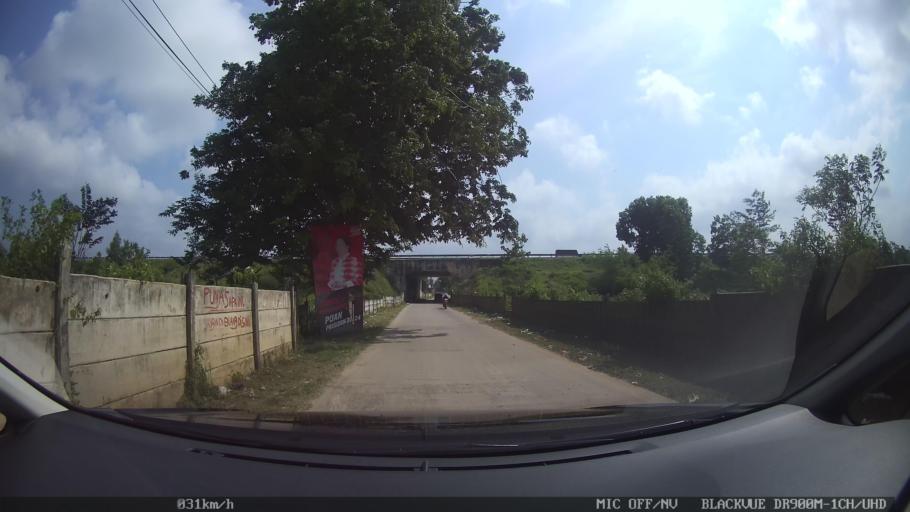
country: ID
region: Lampung
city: Kedaton
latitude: -5.3281
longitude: 105.2831
